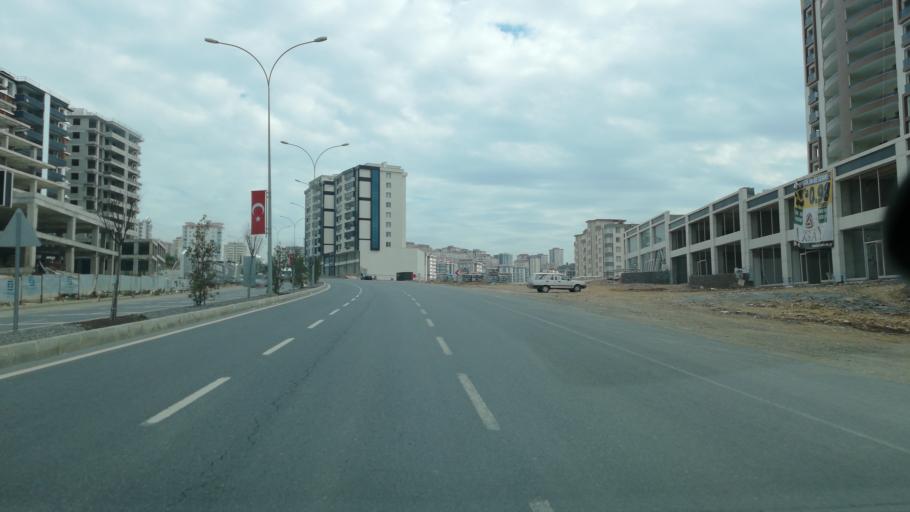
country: TR
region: Kahramanmaras
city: Kahramanmaras
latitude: 37.5852
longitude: 36.8508
